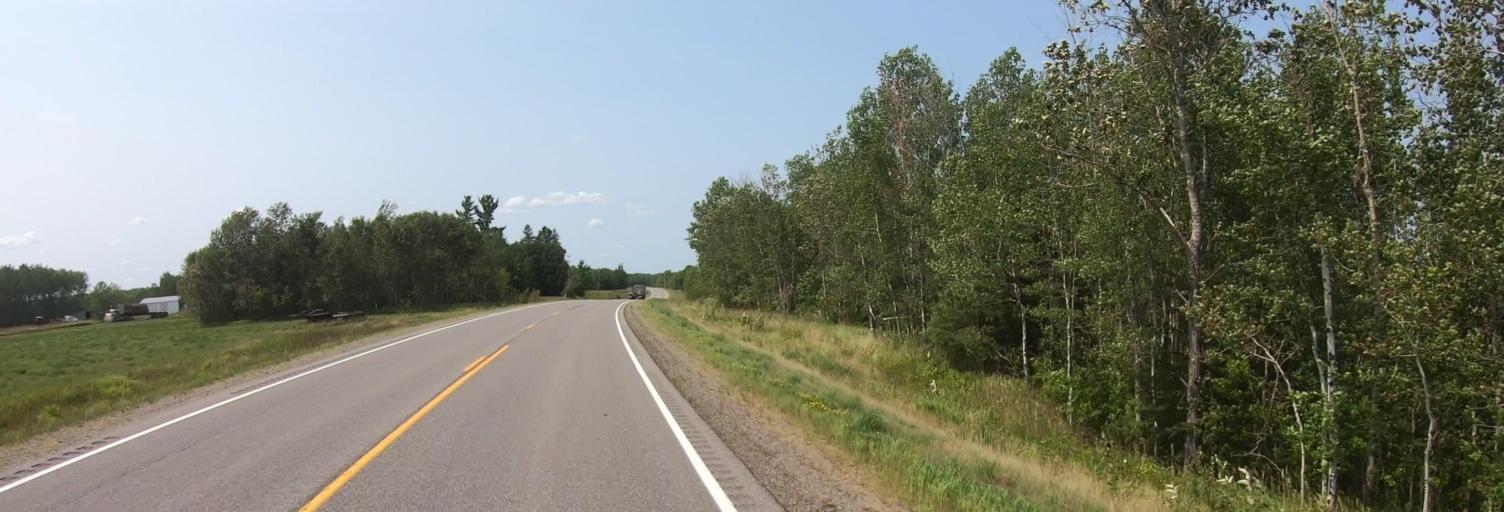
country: US
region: Minnesota
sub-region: Koochiching County
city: International Falls
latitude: 48.6296
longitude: -93.8878
